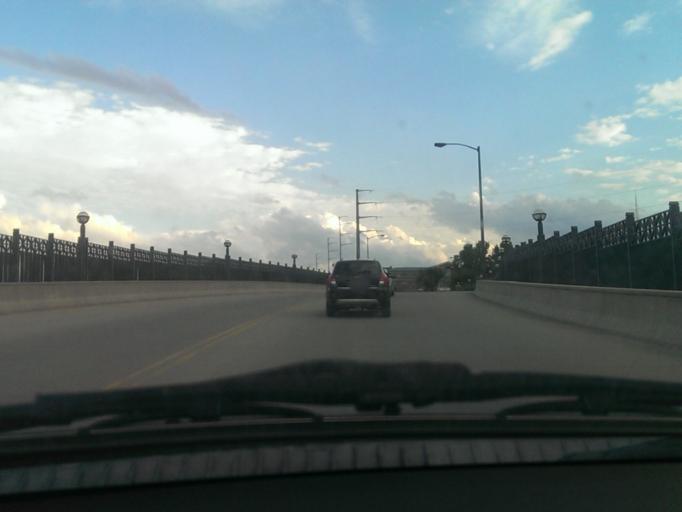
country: US
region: Missouri
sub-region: Jackson County
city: Kansas City
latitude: 39.0868
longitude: -94.5702
